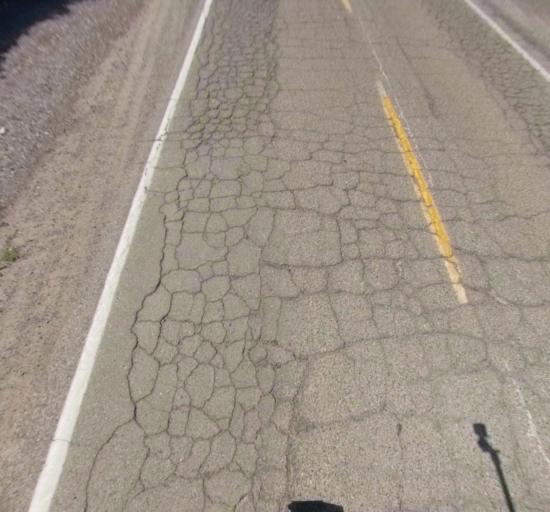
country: US
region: California
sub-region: Madera County
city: Madera
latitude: 36.9316
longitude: -120.2015
